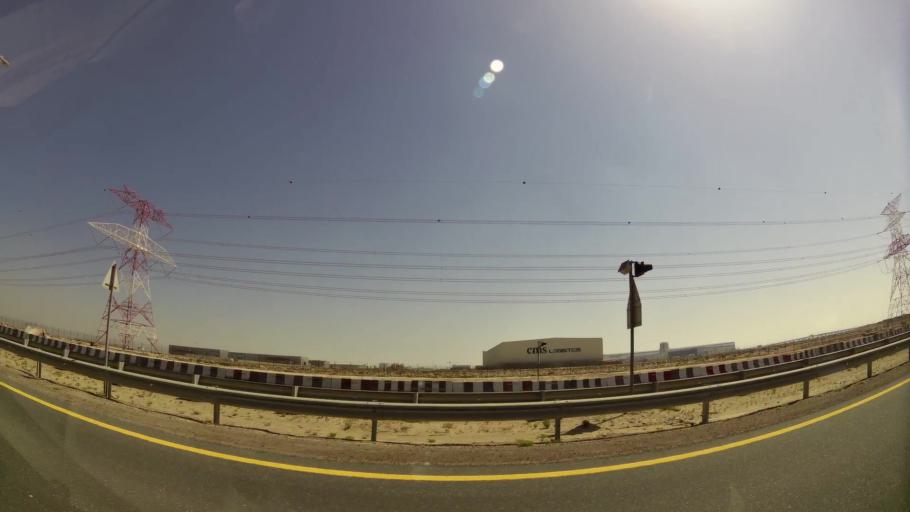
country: AE
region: Dubai
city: Dubai
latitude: 24.9237
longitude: 55.0972
